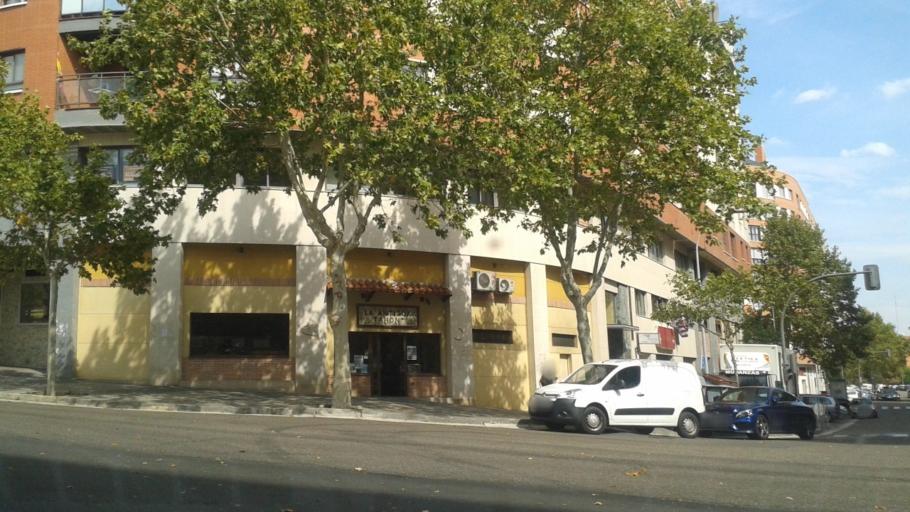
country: ES
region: Castille and Leon
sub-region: Provincia de Valladolid
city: Zaratan
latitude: 41.6350
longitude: -4.7599
